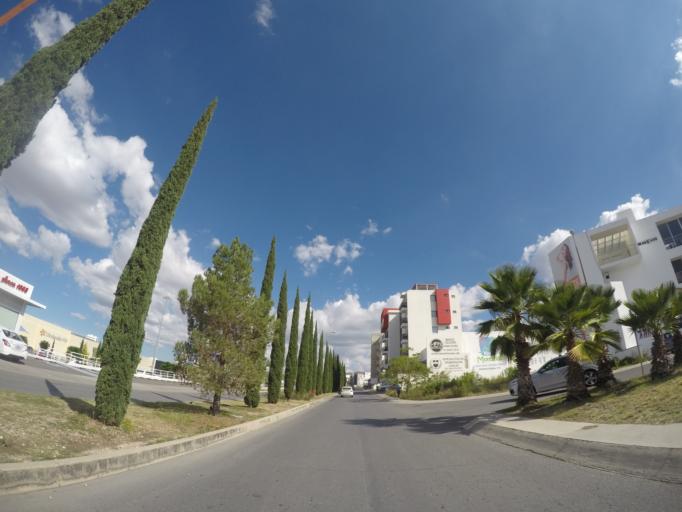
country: MX
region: San Luis Potosi
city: Escalerillas
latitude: 22.1268
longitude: -101.0324
